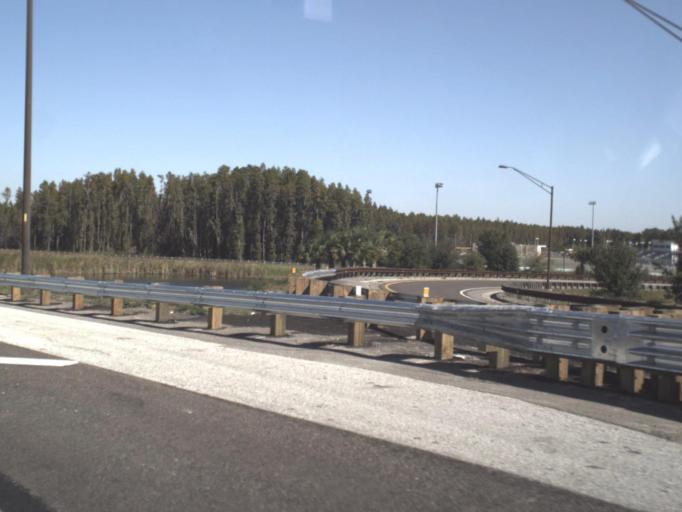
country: US
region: Florida
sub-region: Hillsborough County
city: Cheval
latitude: 28.1575
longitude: -82.5378
